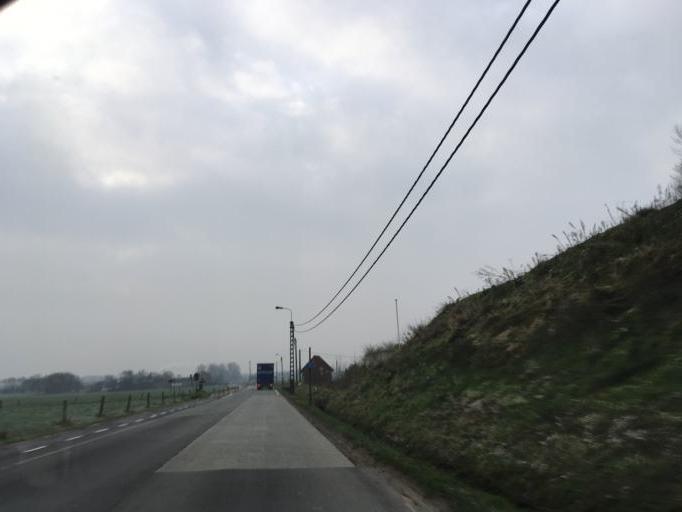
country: BE
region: Flanders
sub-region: Provincie West-Vlaanderen
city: Oostrozebeke
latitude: 50.9431
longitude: 3.3360
